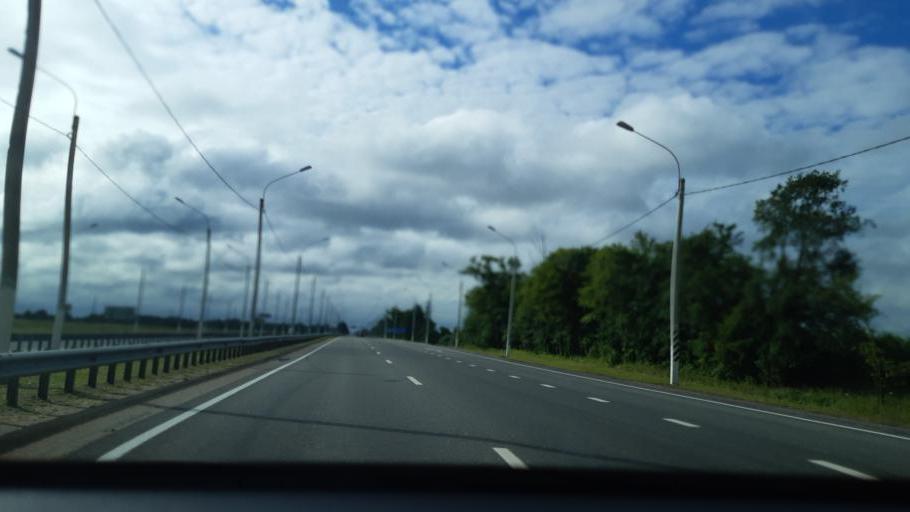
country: RU
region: Smolensk
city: Talashkino
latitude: 54.7005
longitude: 32.1226
